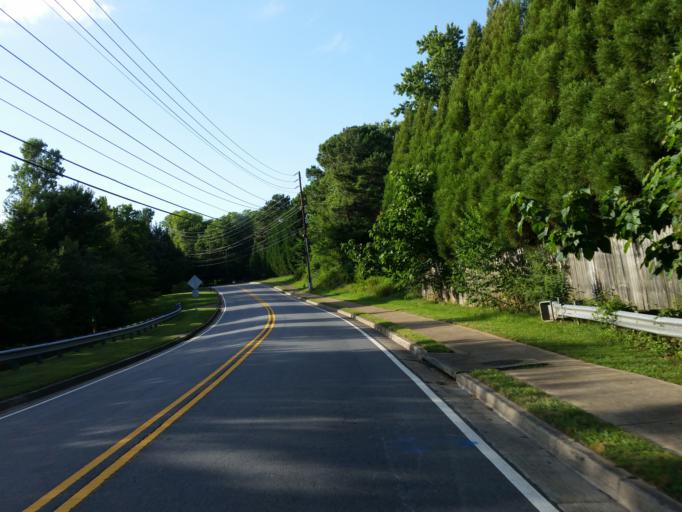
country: US
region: Georgia
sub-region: Cherokee County
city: Woodstock
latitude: 34.0711
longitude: -84.4837
